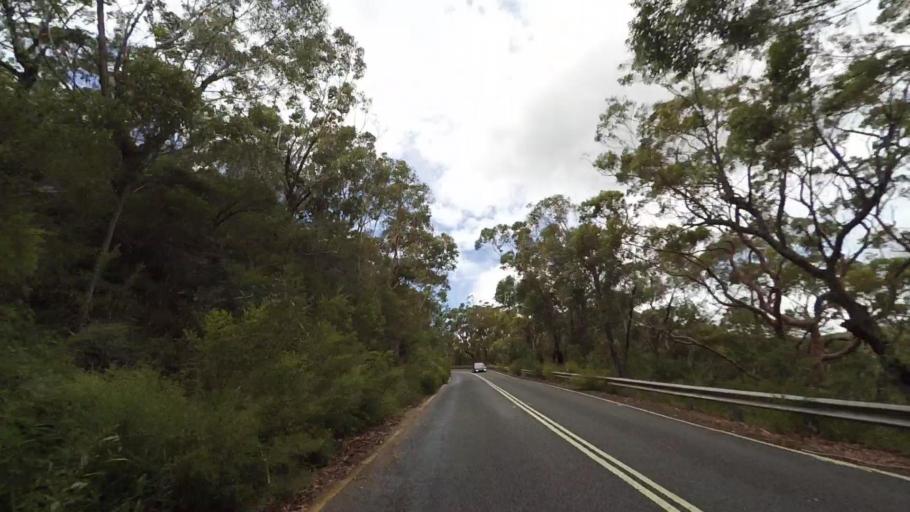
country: AU
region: New South Wales
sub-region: Sutherland Shire
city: Grays Point
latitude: -34.0813
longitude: 151.0589
